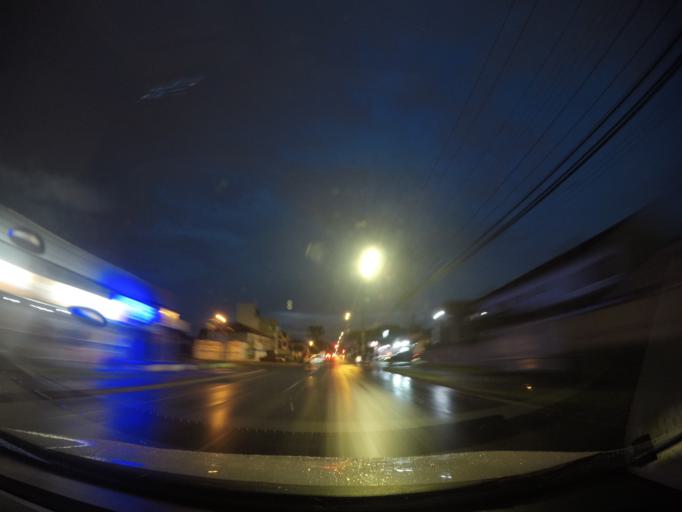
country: BR
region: Parana
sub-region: Curitiba
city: Curitiba
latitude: -25.4803
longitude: -49.2548
